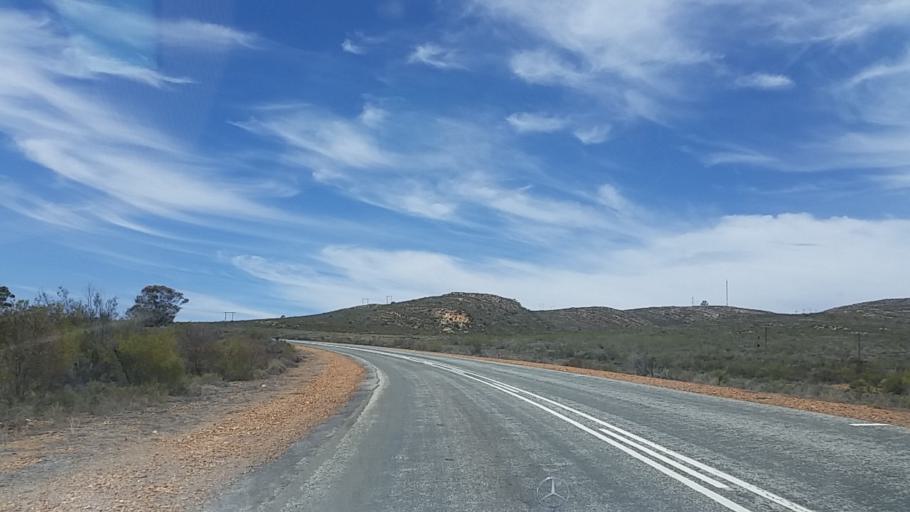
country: ZA
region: Western Cape
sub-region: Eden District Municipality
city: Knysna
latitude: -33.7111
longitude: 23.0440
